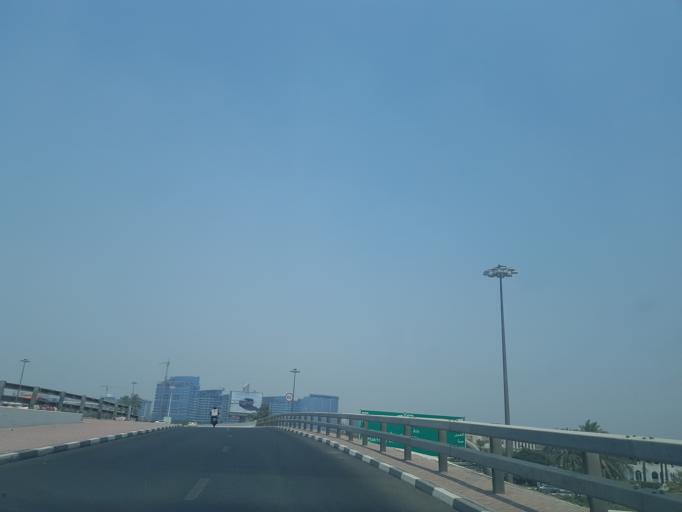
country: AE
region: Ash Shariqah
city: Sharjah
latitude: 25.2483
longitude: 55.3170
